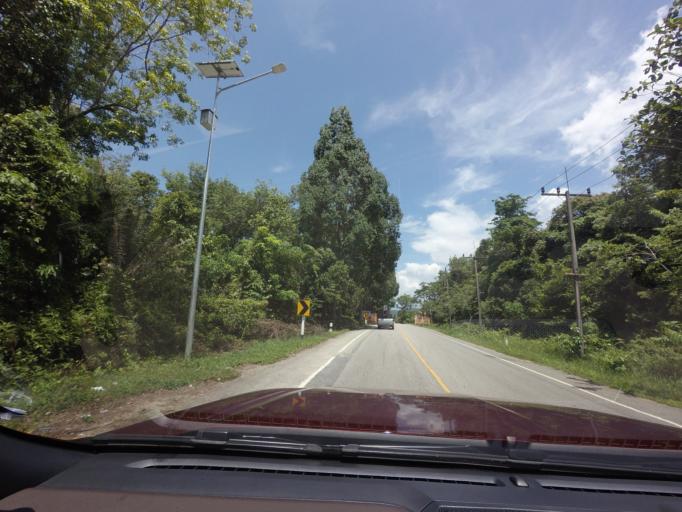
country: TH
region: Narathiwat
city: Chanae
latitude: 6.1377
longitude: 101.7009
